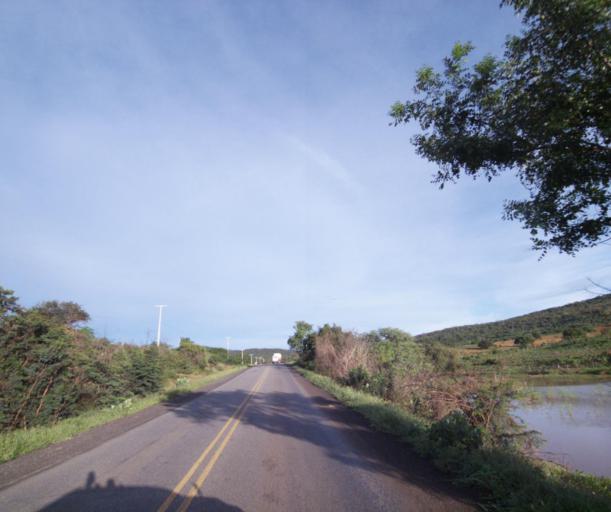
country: BR
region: Bahia
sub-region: Cacule
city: Cacule
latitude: -14.1913
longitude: -42.1557
